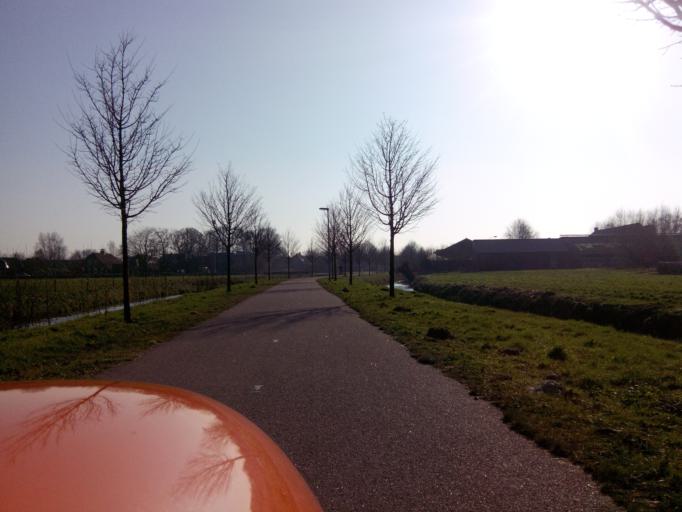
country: NL
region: Gelderland
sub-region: Gemeente Nijkerk
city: Nijkerk
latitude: 52.2228
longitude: 5.4617
